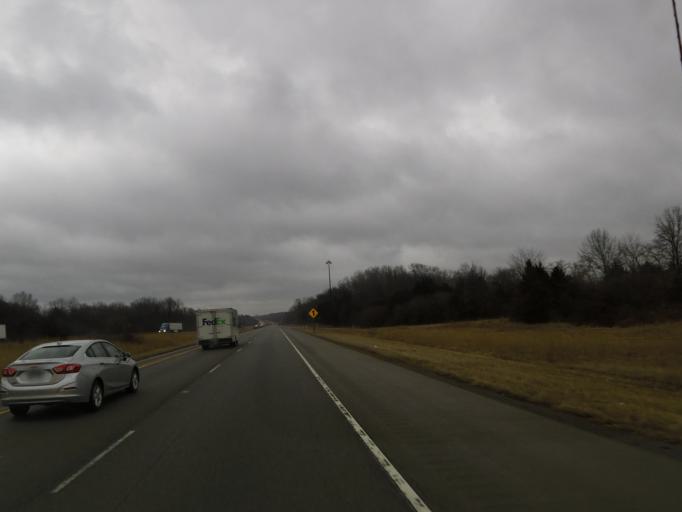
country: US
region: Illinois
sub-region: Johnson County
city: Goreville
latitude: 37.6010
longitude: -88.9947
